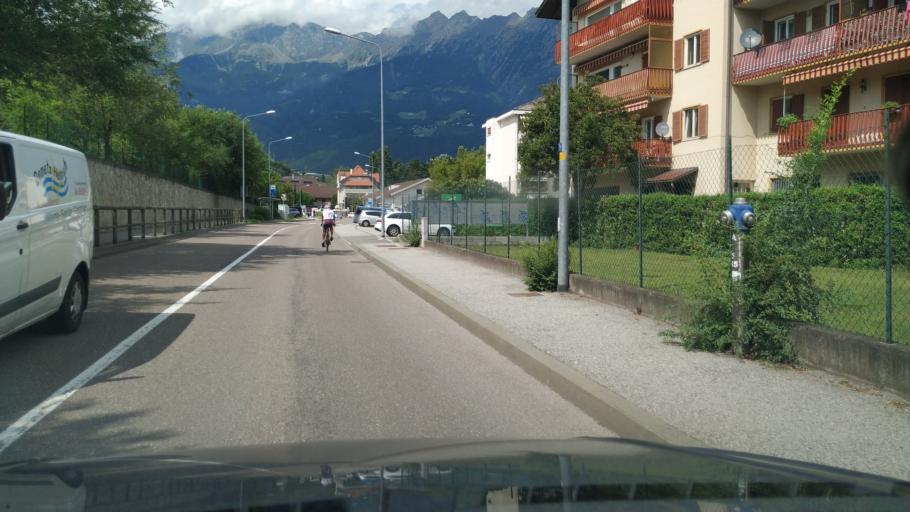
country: IT
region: Trentino-Alto Adige
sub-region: Bolzano
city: Marlengo
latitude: 46.6547
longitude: 11.1509
